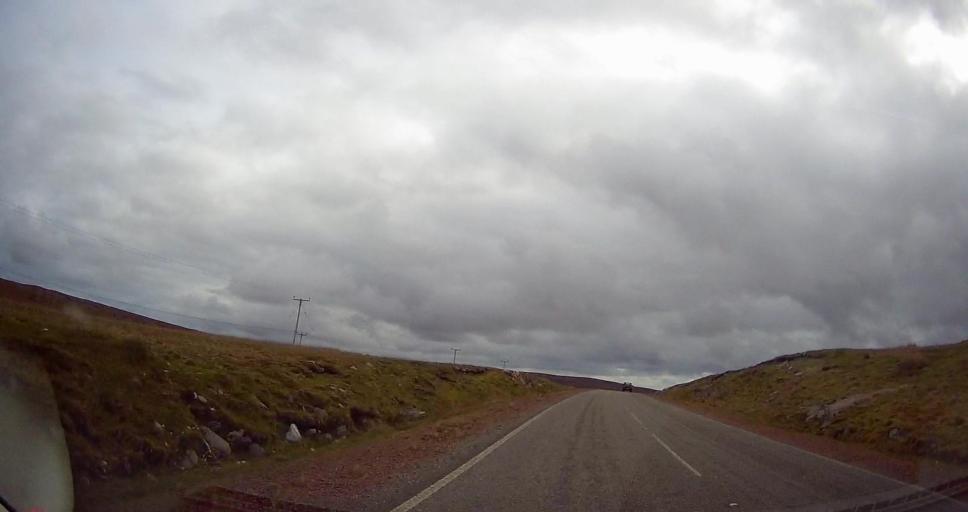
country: GB
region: Scotland
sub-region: Shetland Islands
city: Shetland
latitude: 60.5990
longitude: -1.1371
